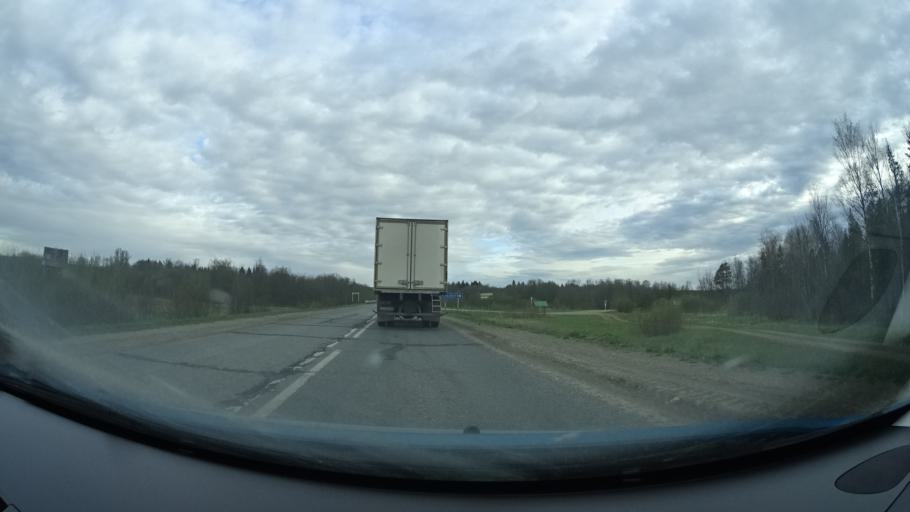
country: RU
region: Perm
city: Yugo-Kamskiy
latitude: 57.5459
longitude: 55.6840
